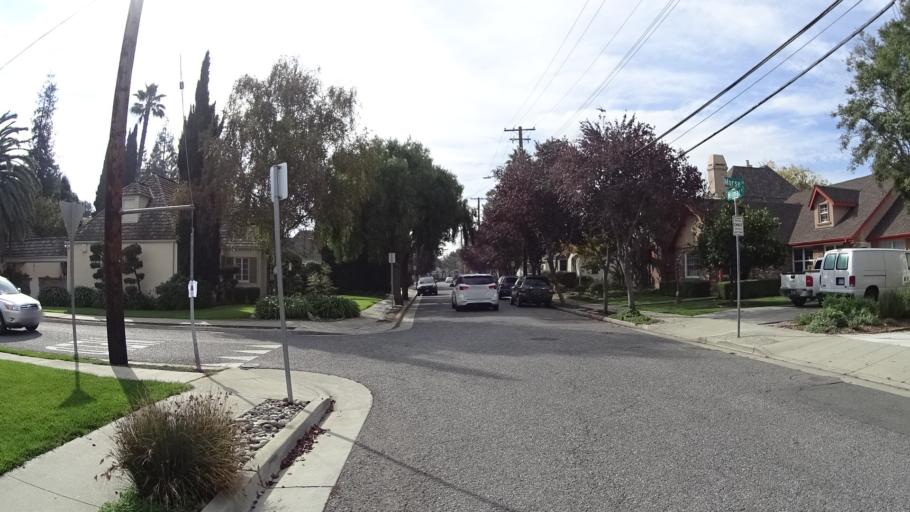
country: US
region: California
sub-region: Santa Clara County
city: Burbank
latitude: 37.3435
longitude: -121.9340
